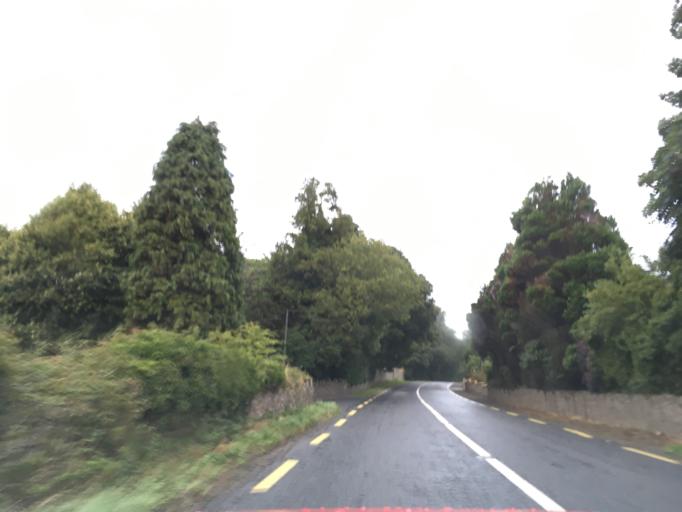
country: IE
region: Munster
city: Tipperary
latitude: 52.4898
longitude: -8.0526
